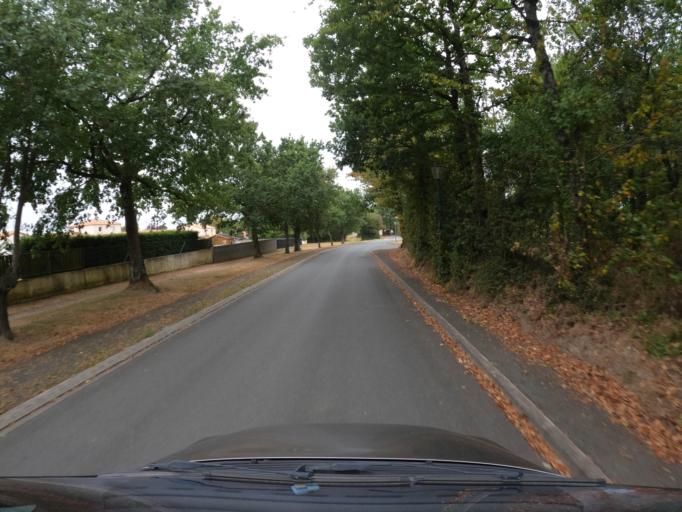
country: FR
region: Pays de la Loire
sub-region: Departement de la Vendee
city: La Guyonniere
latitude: 46.9678
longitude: -1.2543
